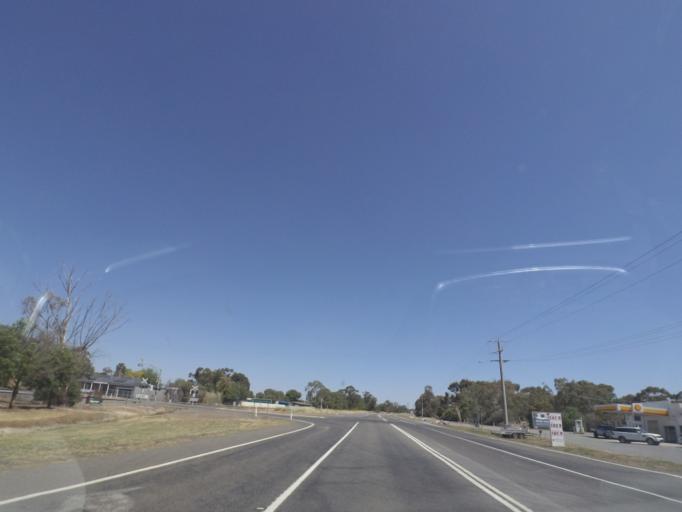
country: AU
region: Victoria
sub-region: Greater Shepparton
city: Shepparton
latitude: -36.2384
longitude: 145.4315
